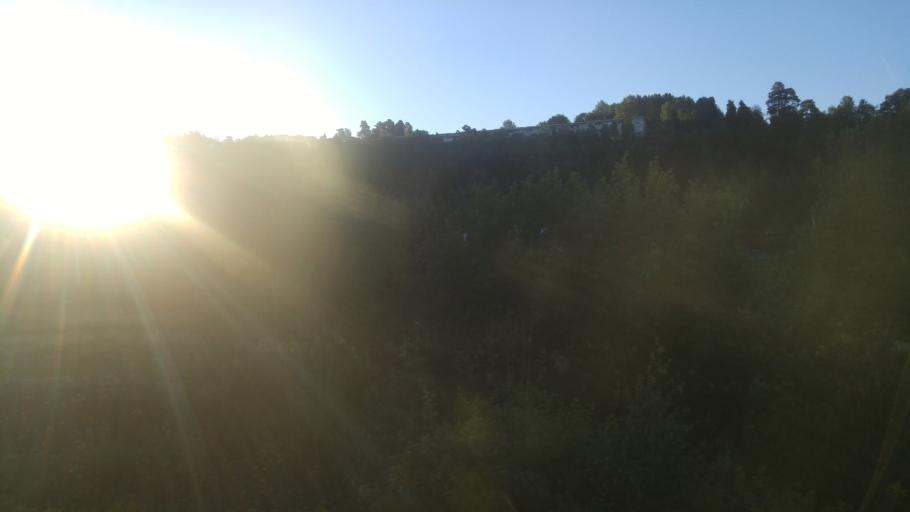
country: NO
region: Oslo
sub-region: Oslo
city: Oslo
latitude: 59.9157
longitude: 10.8289
